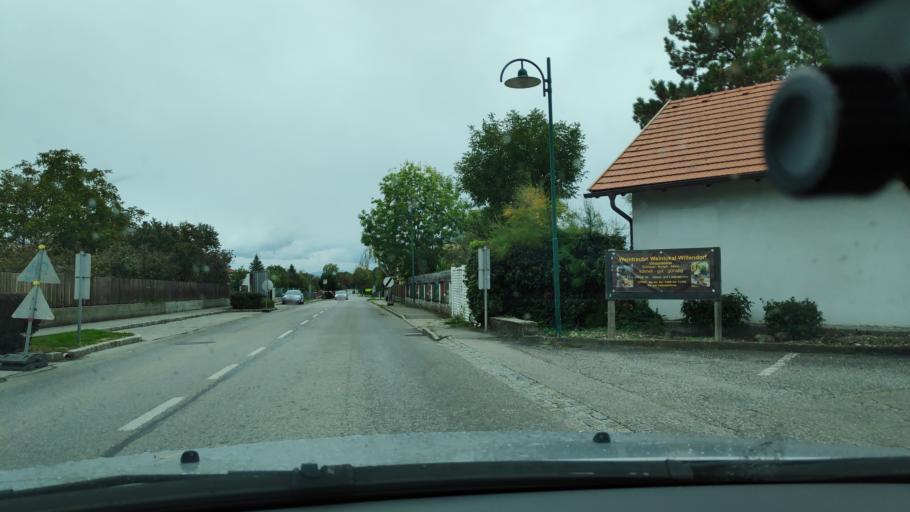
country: AT
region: Lower Austria
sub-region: Politischer Bezirk Neunkirchen
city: Willendorf am Steinfelde
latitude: 47.7882
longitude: 16.0577
